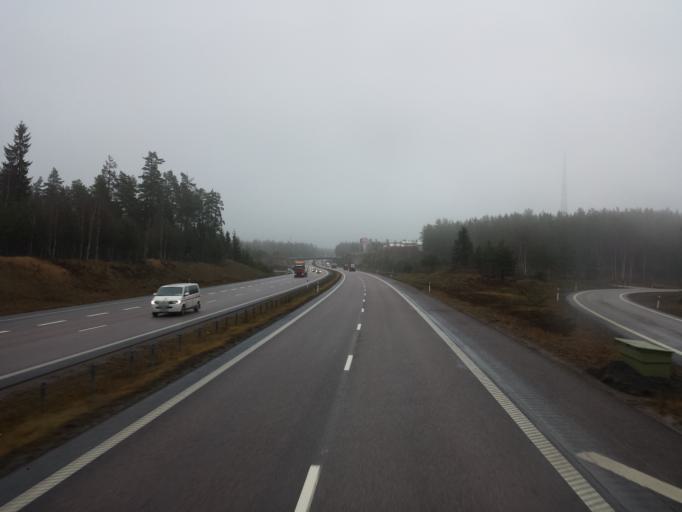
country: SE
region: OEstergoetland
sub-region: Norrkopings Kommun
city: Krokek
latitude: 58.7271
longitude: 16.4028
